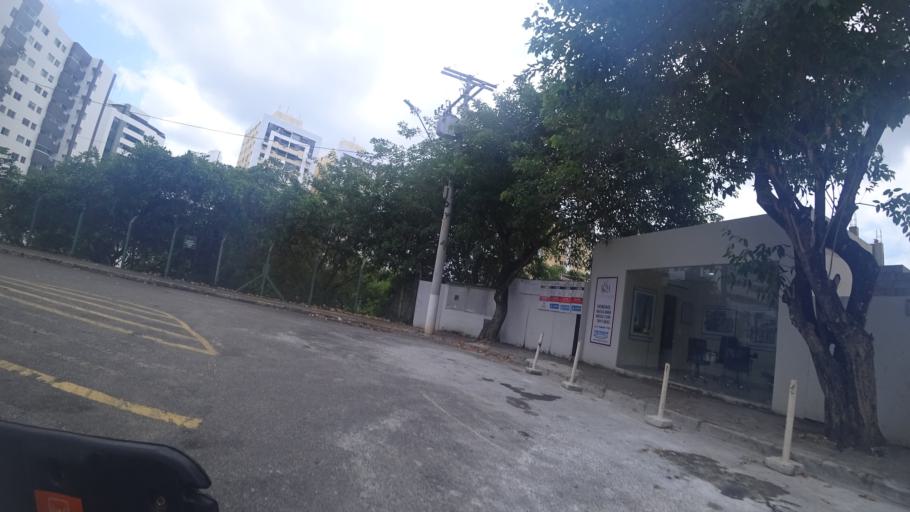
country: BR
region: Bahia
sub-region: Salvador
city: Salvador
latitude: -13.0008
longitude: -38.4670
